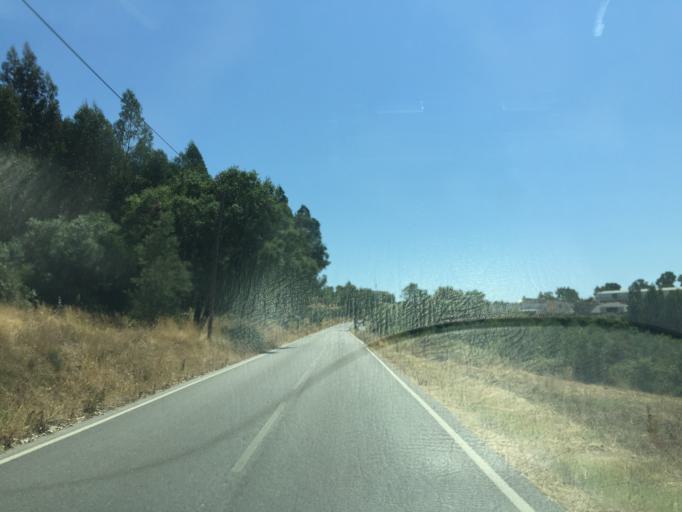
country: PT
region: Santarem
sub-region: Ferreira do Zezere
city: Ferreira do Zezere
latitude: 39.6028
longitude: -8.3104
